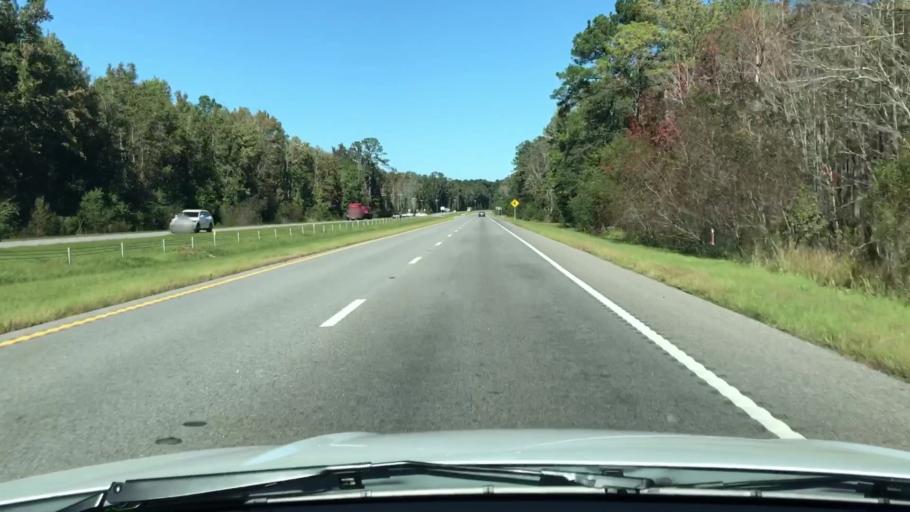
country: US
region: South Carolina
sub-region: Colleton County
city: Walterboro
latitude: 32.7226
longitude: -80.6018
